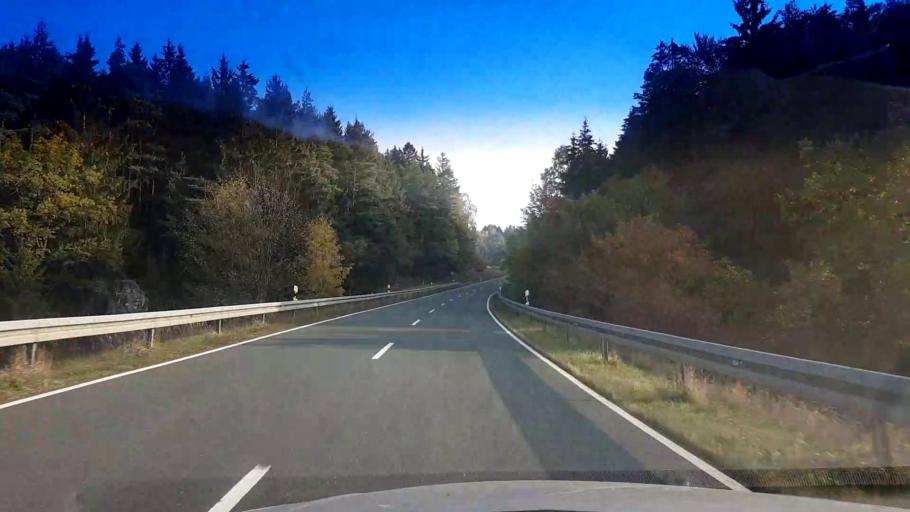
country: DE
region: Bavaria
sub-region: Upper Franconia
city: Stadelhofen
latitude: 50.0038
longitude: 11.1650
